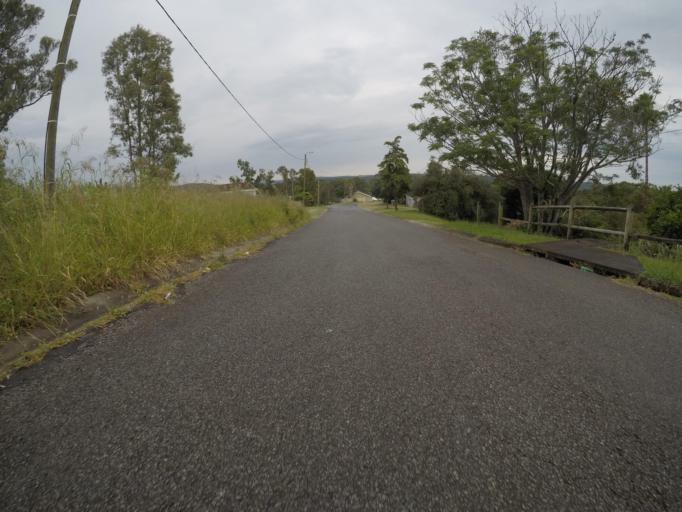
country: ZA
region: Eastern Cape
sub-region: Buffalo City Metropolitan Municipality
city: East London
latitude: -32.9643
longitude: 27.8487
